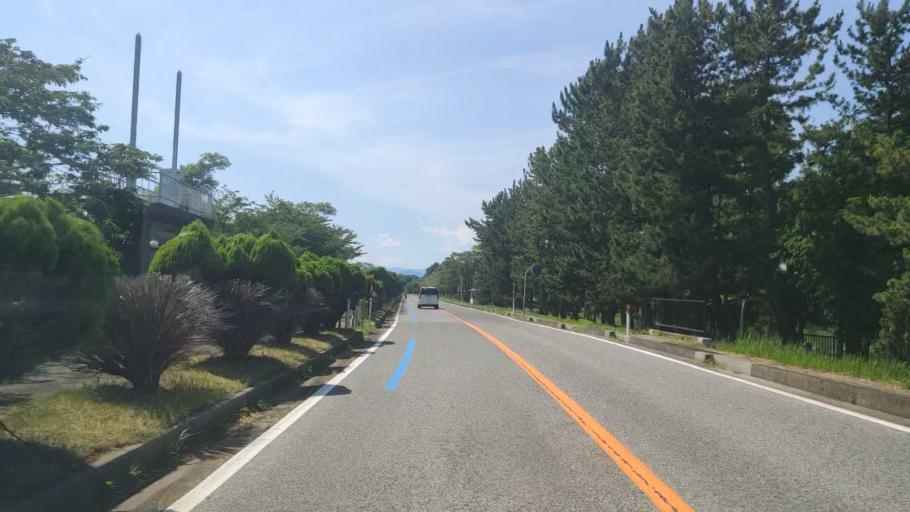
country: JP
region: Shiga Prefecture
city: Nagahama
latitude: 35.4109
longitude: 136.2091
